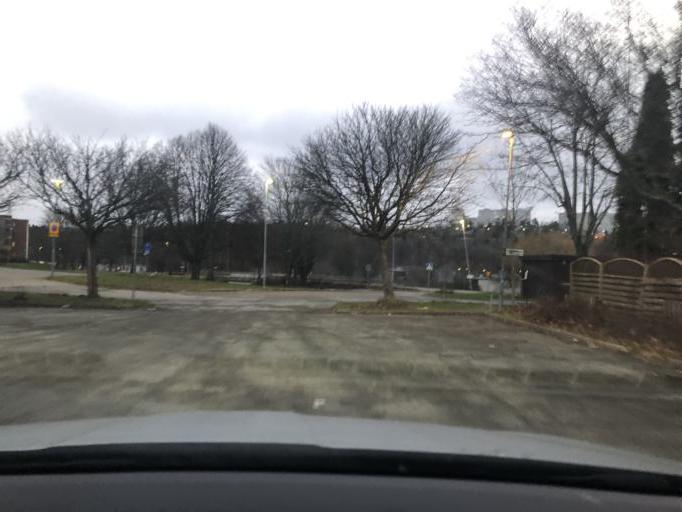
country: SE
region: Stockholm
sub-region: Botkyrka Kommun
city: Fittja
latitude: 59.2483
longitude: 17.8519
